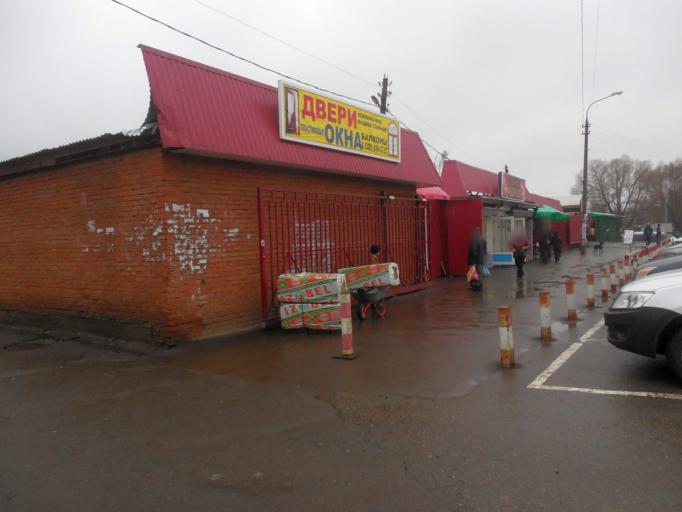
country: RU
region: Moskovskaya
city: Barybino
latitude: 55.2680
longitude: 37.8948
